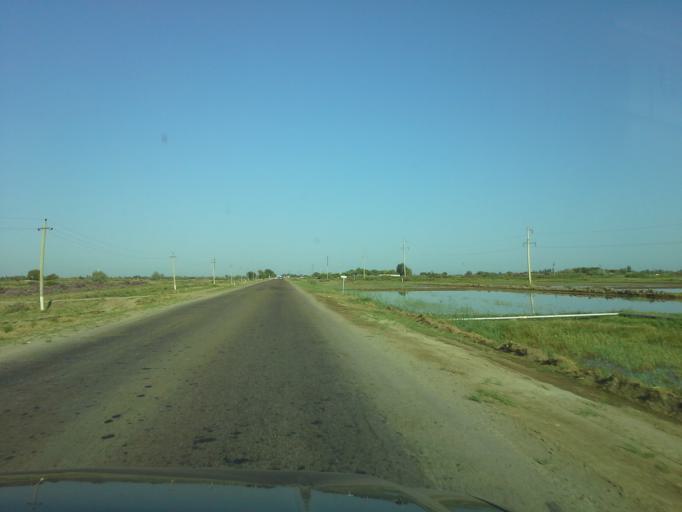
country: UZ
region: Karakalpakstan
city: Khujayli
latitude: 42.2269
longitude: 59.4741
